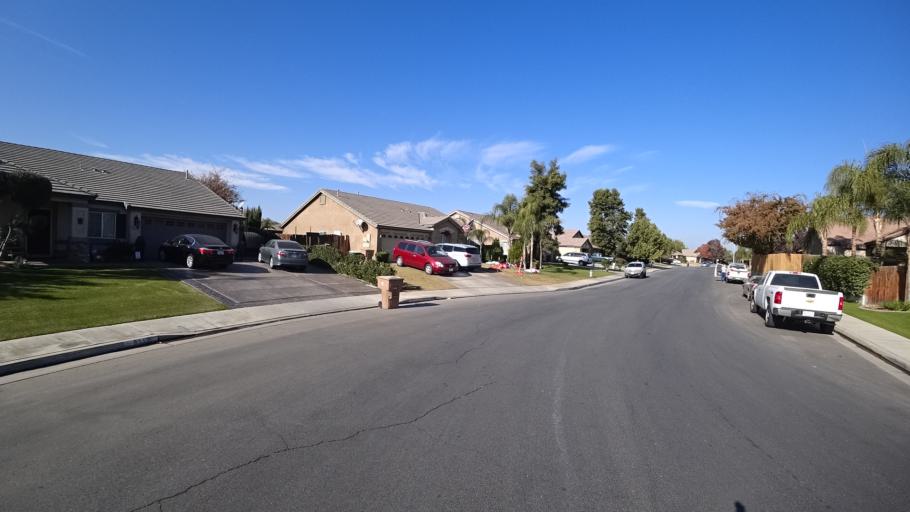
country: US
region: California
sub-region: Kern County
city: Greenfield
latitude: 35.2713
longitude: -119.0612
